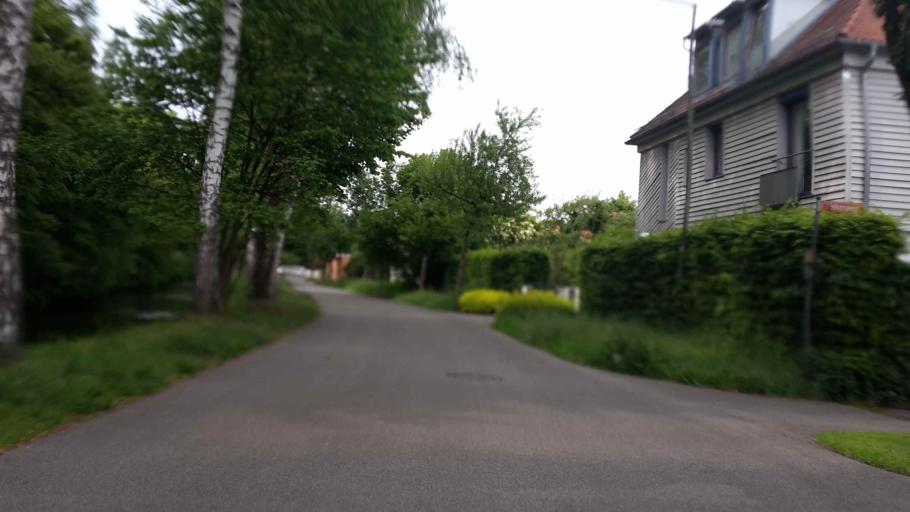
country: DE
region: Bavaria
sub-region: Upper Bavaria
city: Dachau
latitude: 48.2422
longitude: 11.4388
